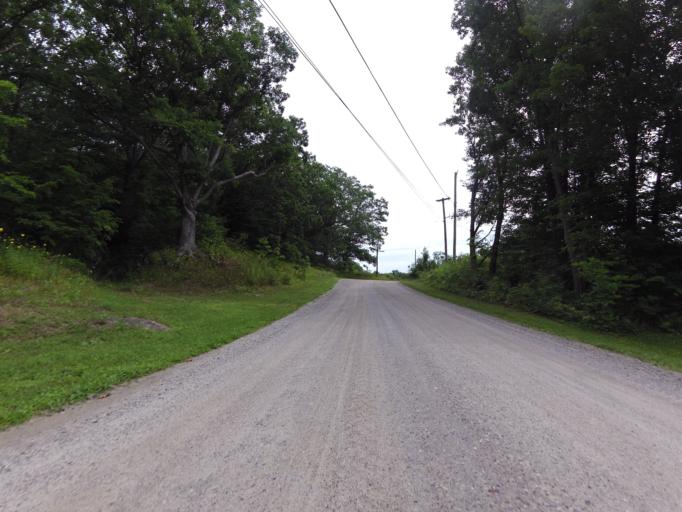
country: CA
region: Ontario
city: Perth
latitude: 44.7337
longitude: -76.6067
